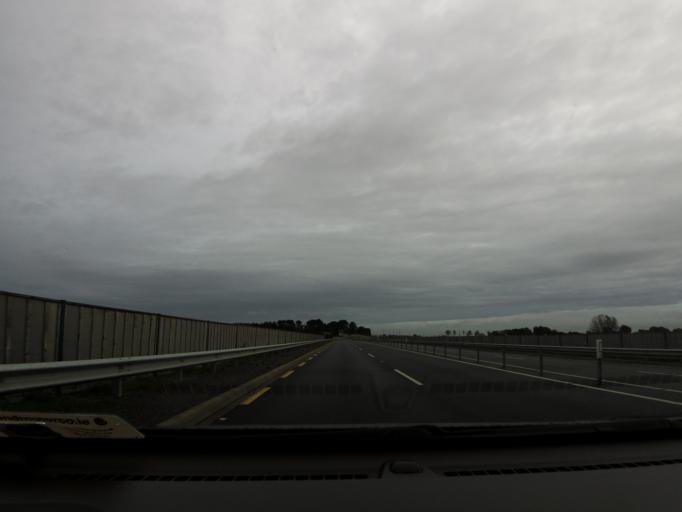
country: IE
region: Connaught
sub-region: County Galway
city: Tuam
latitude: 53.5210
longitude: -8.8773
